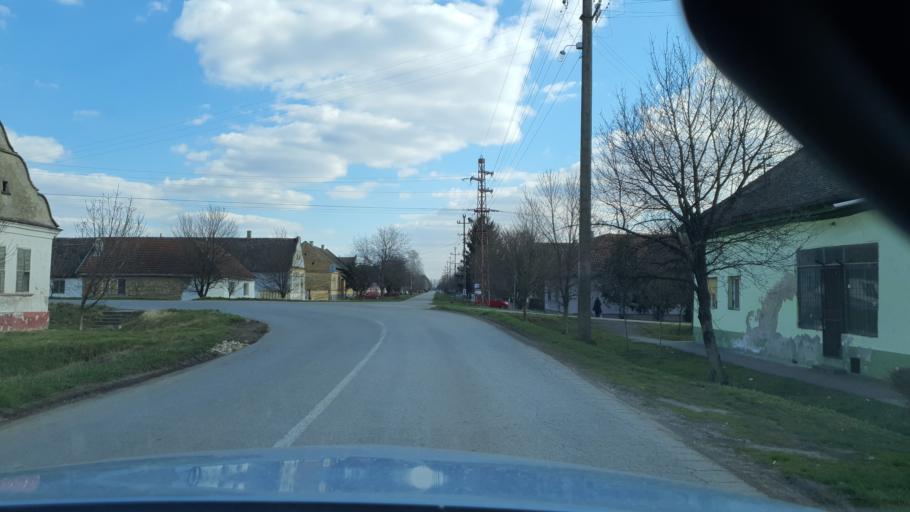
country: RS
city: Ravno Selo
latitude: 45.4476
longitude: 19.6226
